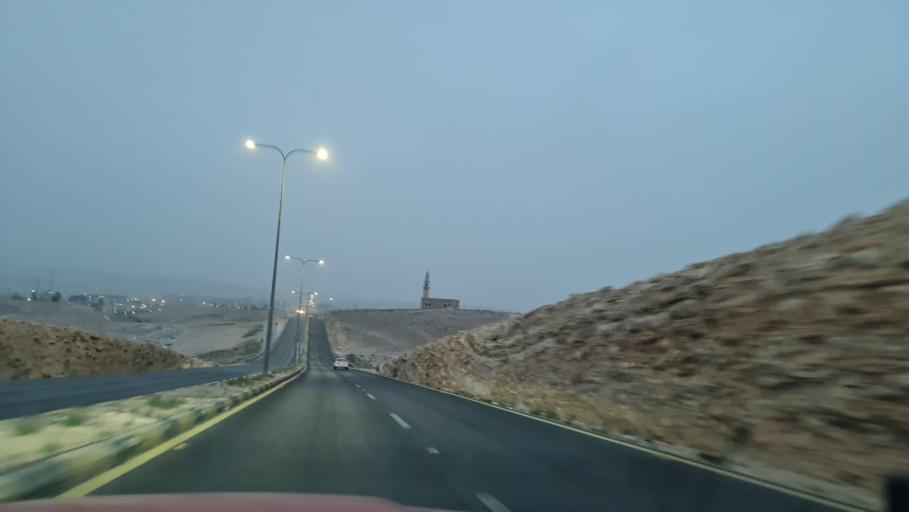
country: JO
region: Zarqa
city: Zarqa
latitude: 32.0457
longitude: 36.1076
